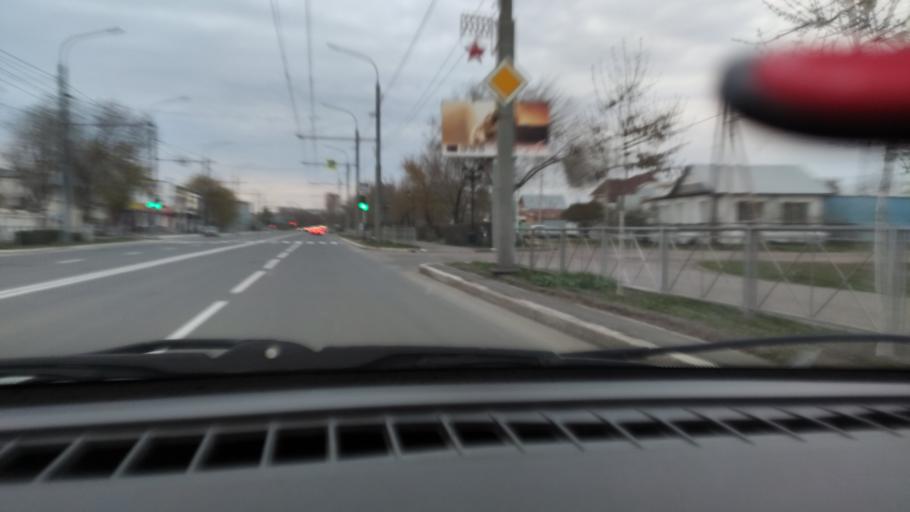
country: RU
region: Orenburg
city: Orenburg
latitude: 51.7832
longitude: 55.1162
